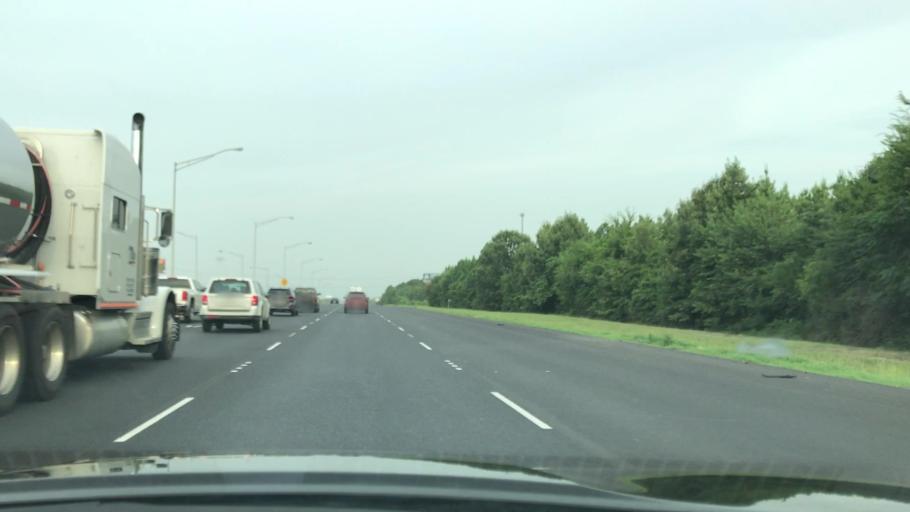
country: US
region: Louisiana
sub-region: Caddo Parish
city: Greenwood
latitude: 32.4499
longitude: -93.8713
